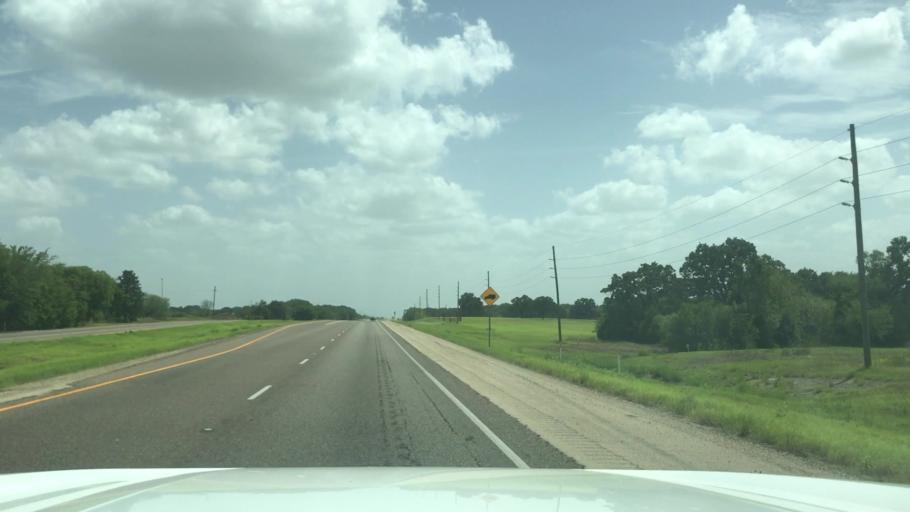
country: US
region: Texas
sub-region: Robertson County
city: Calvert
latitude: 31.0945
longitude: -96.7150
